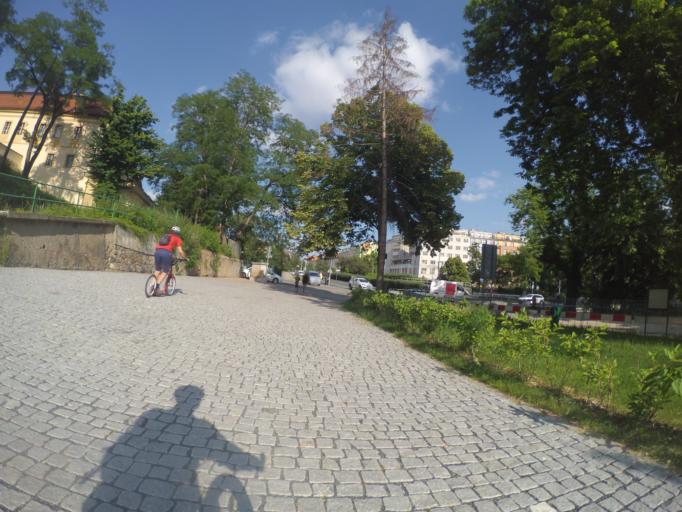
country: CZ
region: Praha
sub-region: Praha 8
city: Liben
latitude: 50.1074
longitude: 14.4704
